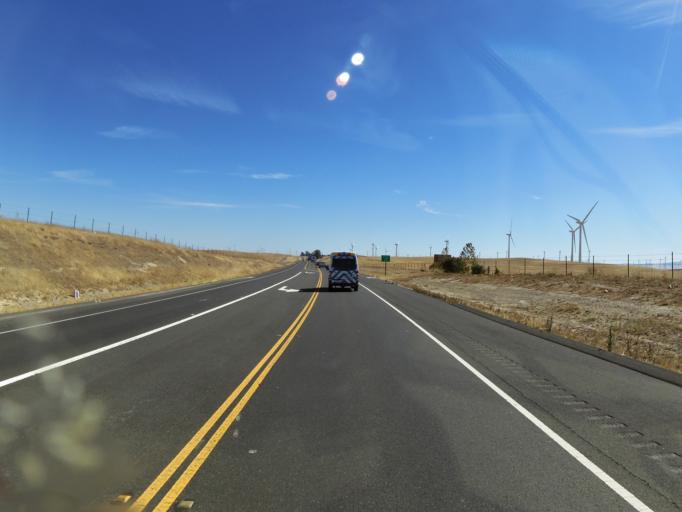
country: US
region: California
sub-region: Solano County
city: Suisun
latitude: 38.2042
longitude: -121.8734
